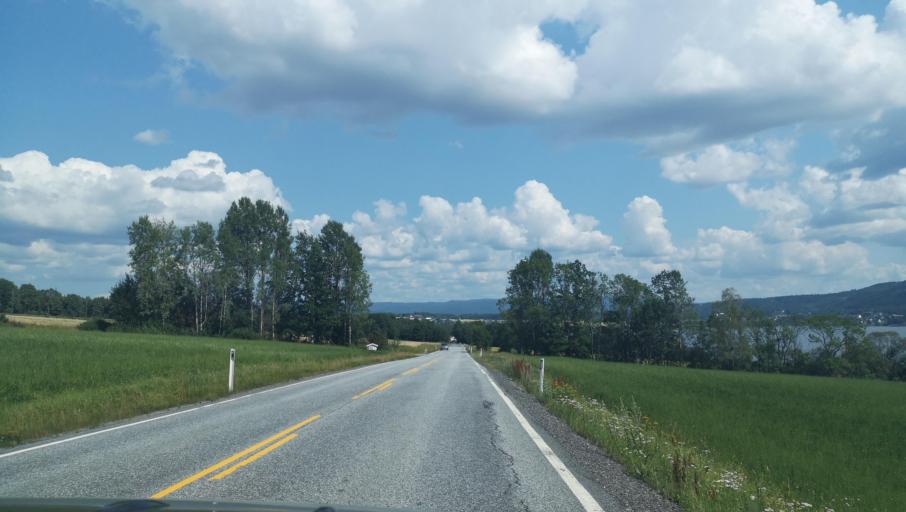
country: NO
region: Buskerud
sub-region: Ovre Eiker
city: Hokksund
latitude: 59.7053
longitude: 9.8092
